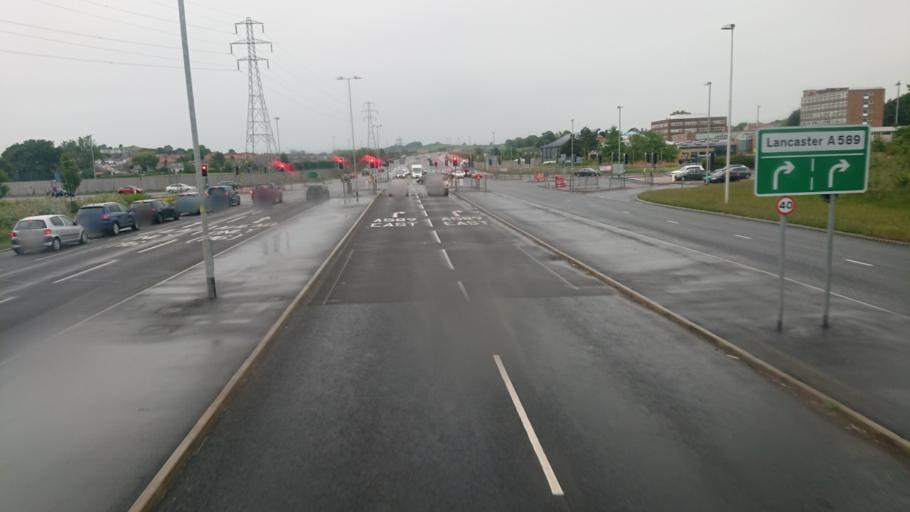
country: GB
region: England
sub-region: Lancashire
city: Morecambe
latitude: 54.0617
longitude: -2.8310
